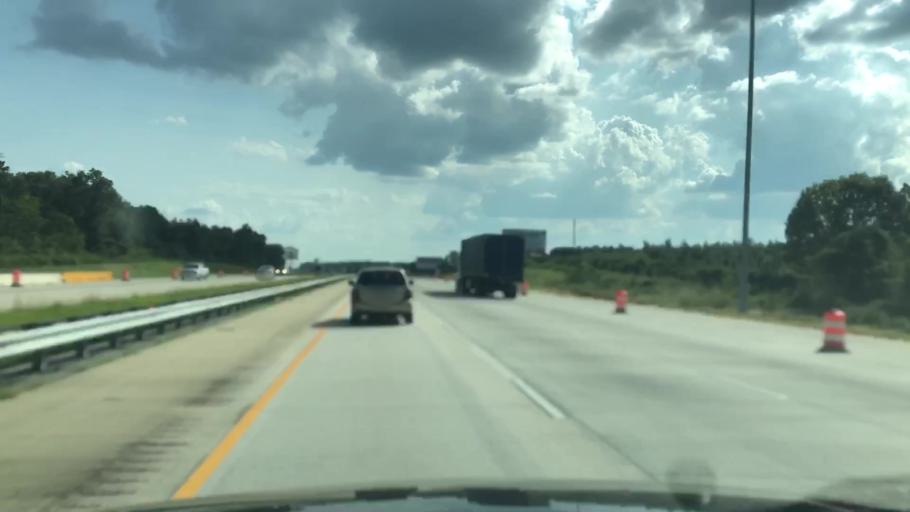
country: US
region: Georgia
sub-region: Dooly County
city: Vienna
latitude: 32.1162
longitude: -83.7628
